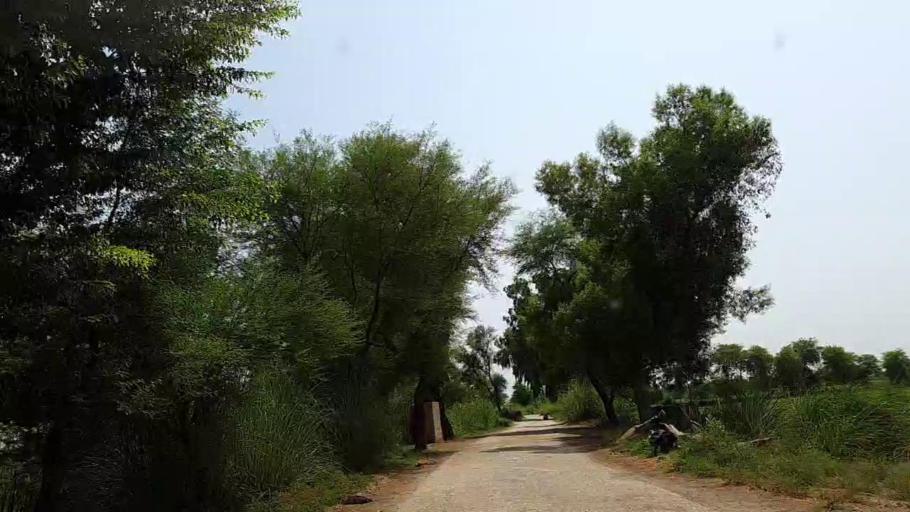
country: PK
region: Sindh
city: Adilpur
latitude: 27.9044
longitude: 69.3626
